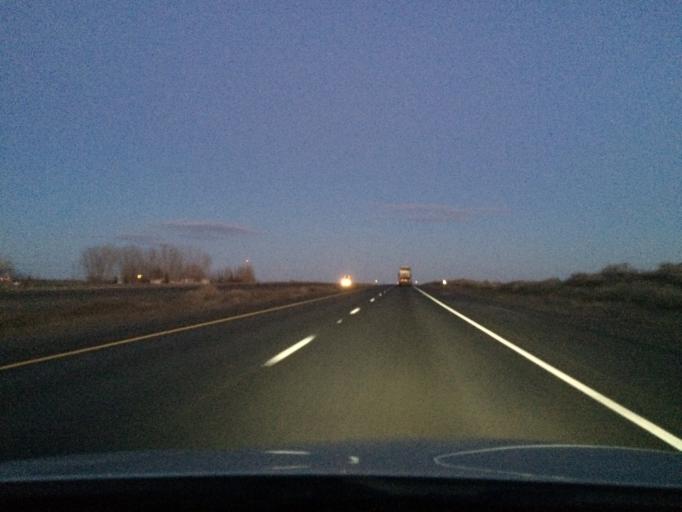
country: US
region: Washington
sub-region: Grant County
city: Cascade Valley
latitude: 47.1039
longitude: -119.4166
